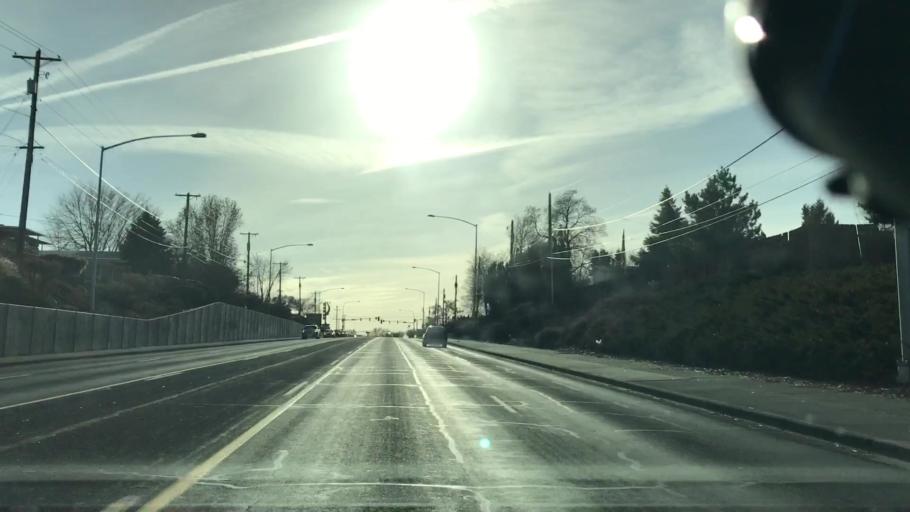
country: US
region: Washington
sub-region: Grant County
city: Moses Lake
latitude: 47.1238
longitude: -119.2684
